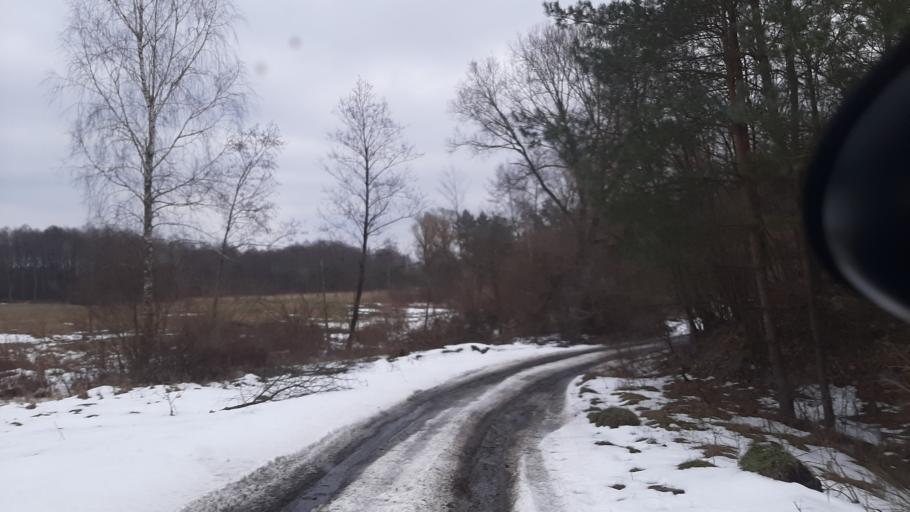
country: PL
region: Lublin Voivodeship
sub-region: Powiat wlodawski
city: Wlodawa
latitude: 51.5137
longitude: 23.6102
